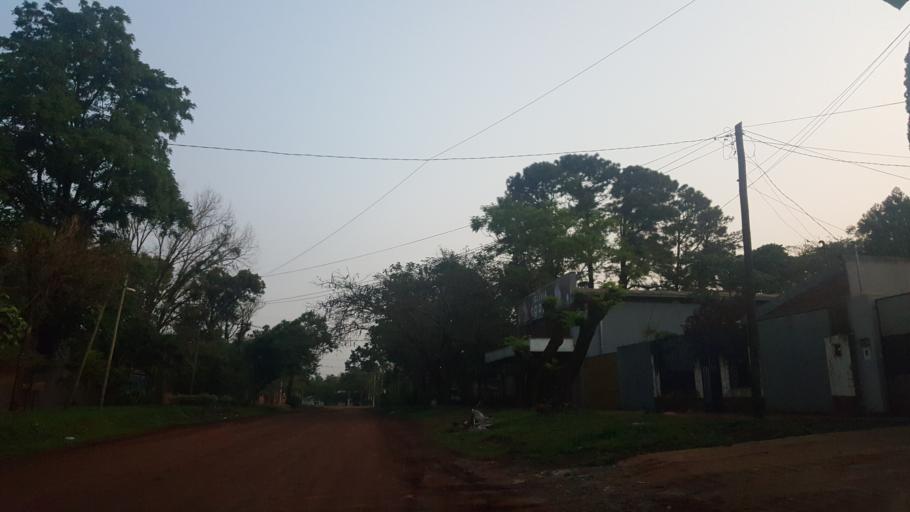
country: AR
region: Misiones
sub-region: Departamento de Capital
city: Posadas
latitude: -27.3987
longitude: -55.9399
